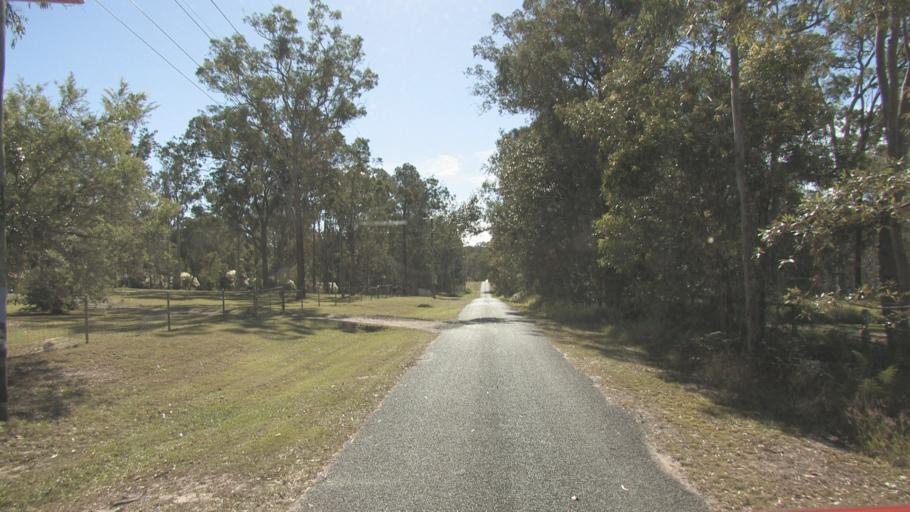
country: AU
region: Queensland
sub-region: Ipswich
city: Springfield Lakes
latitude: -27.7137
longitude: 152.9383
